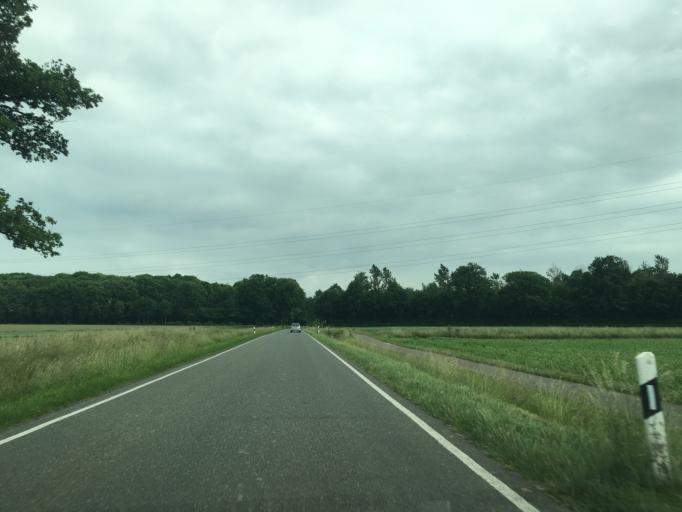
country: DE
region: North Rhine-Westphalia
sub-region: Regierungsbezirk Munster
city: Horstmar
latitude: 52.1040
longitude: 7.3149
